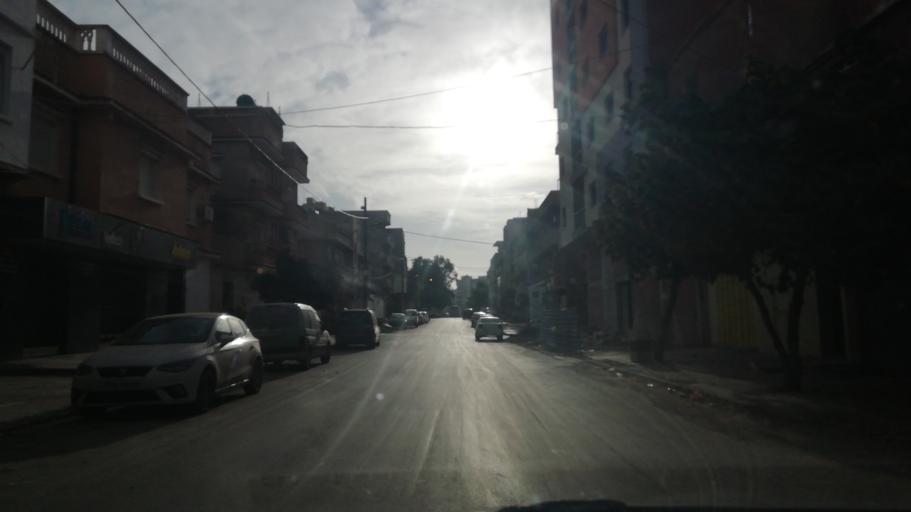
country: DZ
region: Oran
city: Bir el Djir
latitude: 35.7282
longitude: -0.5821
